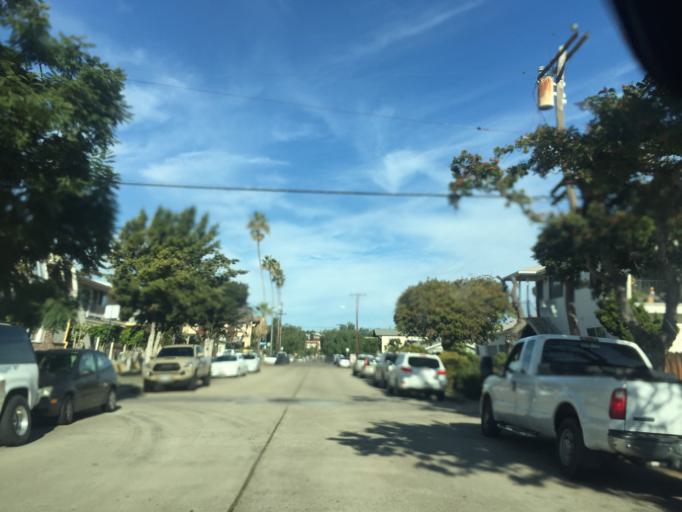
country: US
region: California
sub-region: San Diego County
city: La Jolla
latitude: 32.7961
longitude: -117.2358
